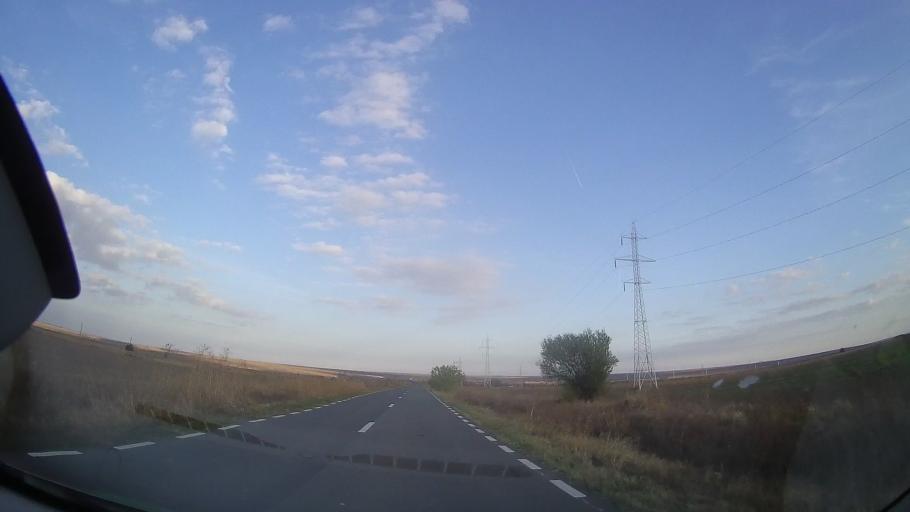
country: RO
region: Constanta
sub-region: Comuna Chirnogeni
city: Plopeni
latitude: 43.9518
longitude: 28.1669
